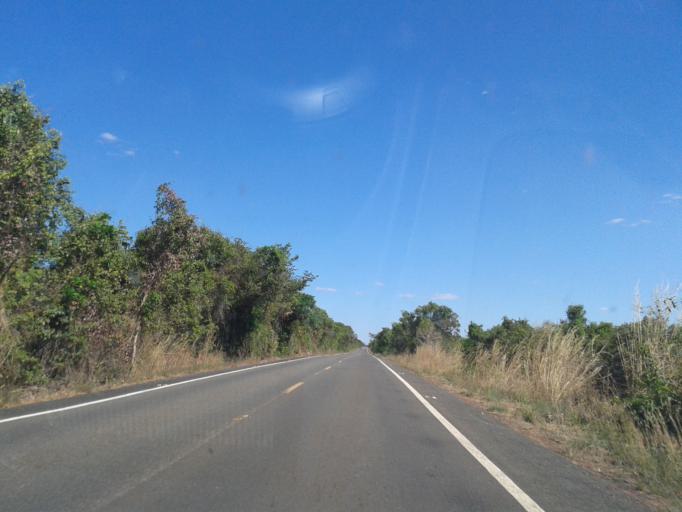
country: BR
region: Goias
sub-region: Sao Miguel Do Araguaia
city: Sao Miguel do Araguaia
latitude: -13.7174
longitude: -50.3338
